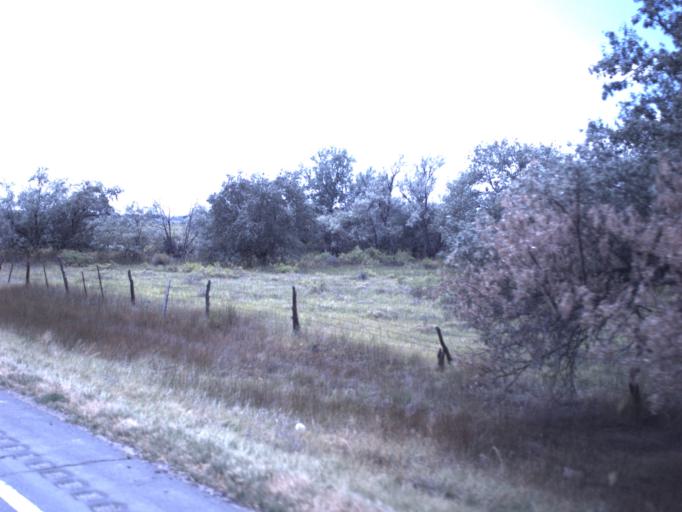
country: US
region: Utah
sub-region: Duchesne County
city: Roosevelt
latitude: 40.1781
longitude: -110.1182
